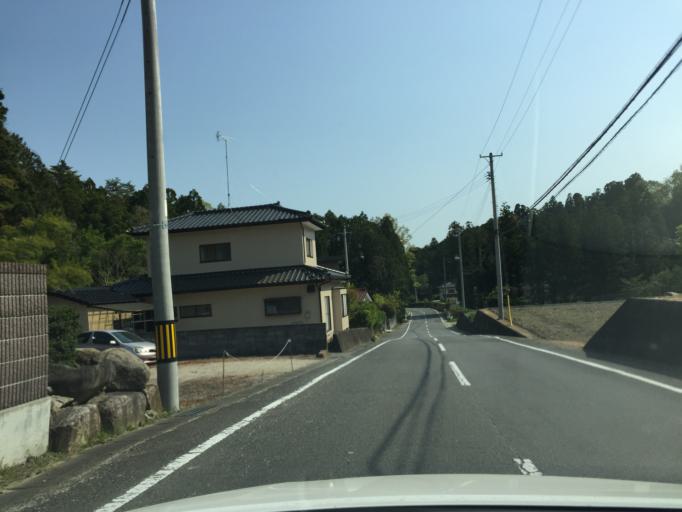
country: JP
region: Fukushima
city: Iwaki
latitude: 37.1418
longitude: 140.8542
